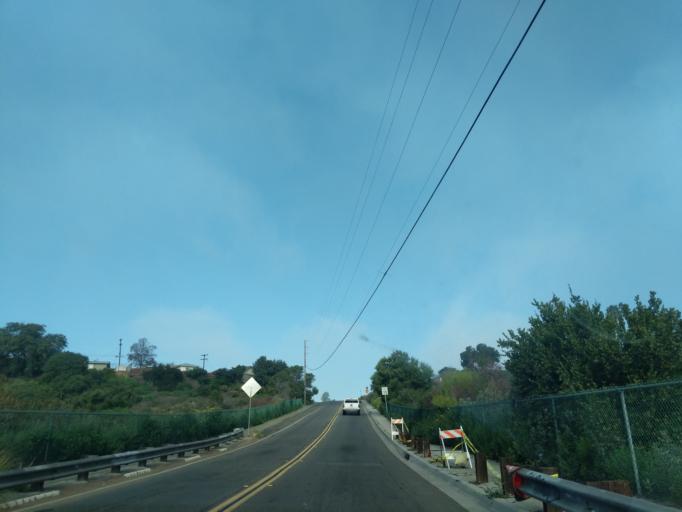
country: US
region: California
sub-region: San Diego County
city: Lemon Grove
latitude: 32.7359
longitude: -117.0877
